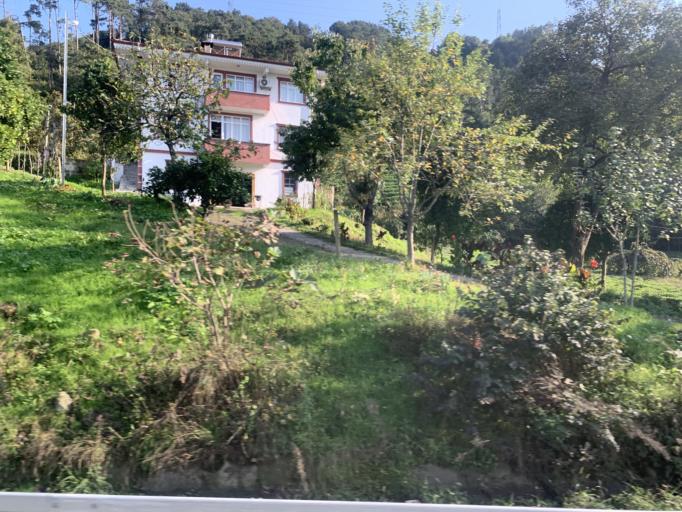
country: TR
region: Trabzon
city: Of
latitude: 40.9310
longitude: 40.2370
